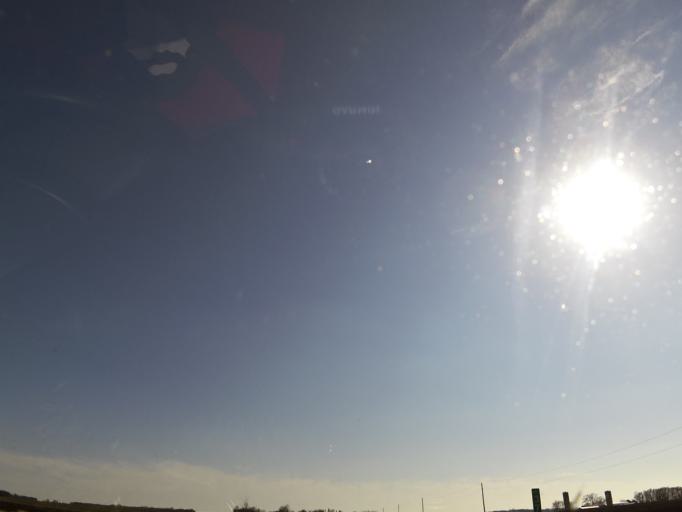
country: US
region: Minnesota
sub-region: Steele County
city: Owatonna
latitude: 44.0158
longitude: -93.2523
